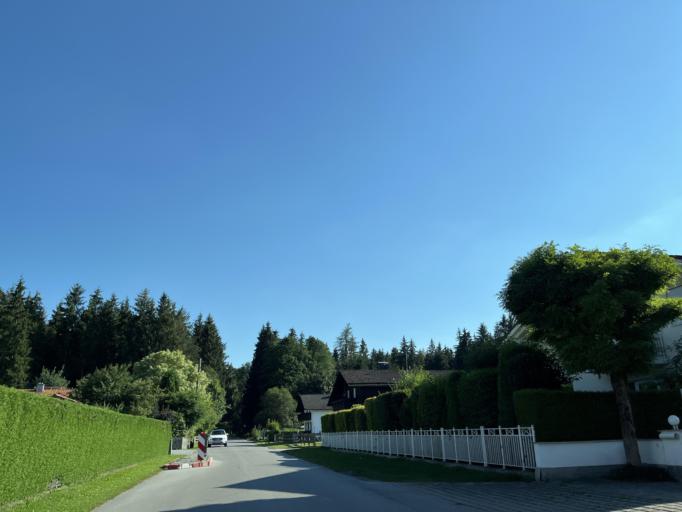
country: DE
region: Bavaria
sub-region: Upper Bavaria
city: Raubling
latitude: 47.7963
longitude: 12.0701
